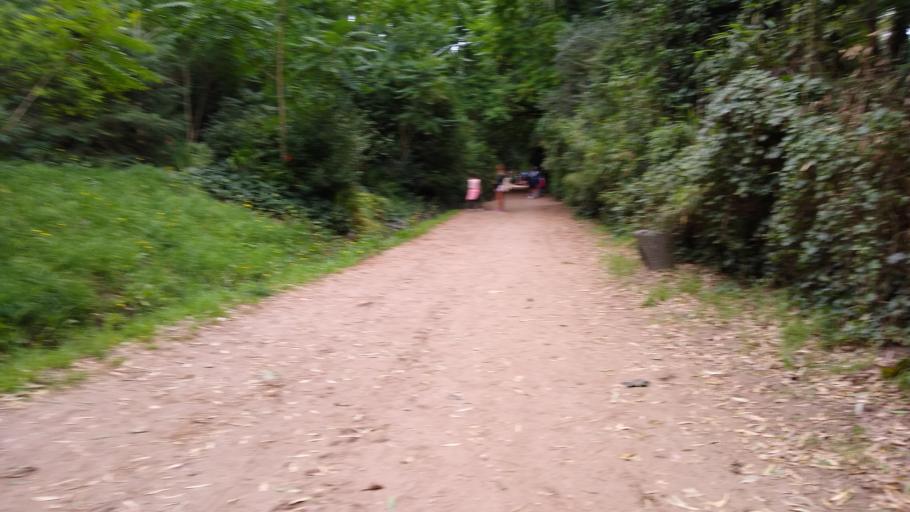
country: AR
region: Buenos Aires
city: Villa Gesell
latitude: -37.2511
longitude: -56.9635
